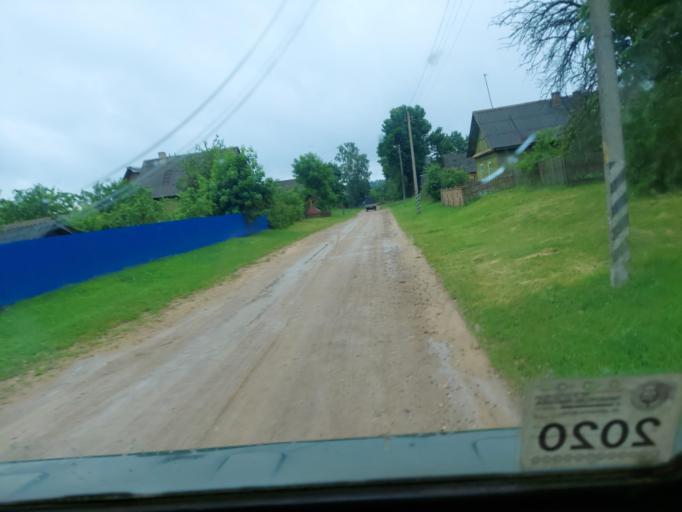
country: BY
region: Mogilev
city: Poselok Voskhod
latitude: 53.6798
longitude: 30.3880
